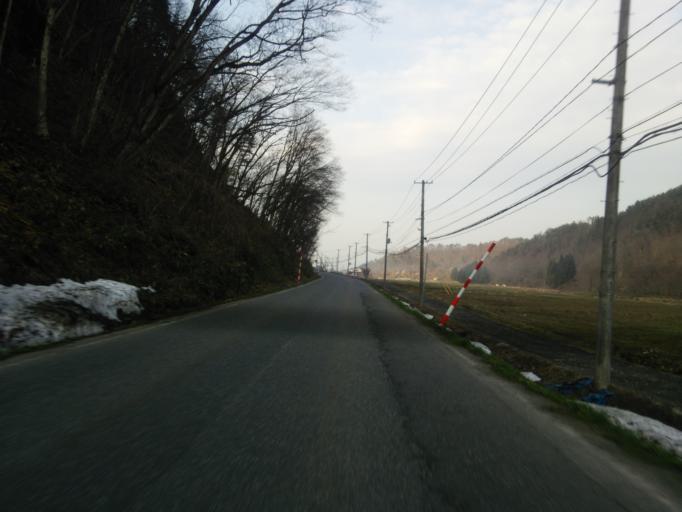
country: JP
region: Fukushima
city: Kitakata
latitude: 37.6929
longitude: 139.9094
